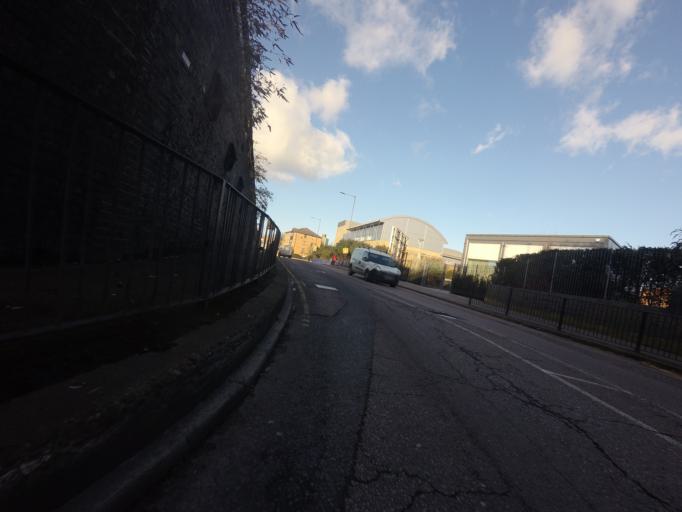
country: GB
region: England
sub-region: Greater London
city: Poplar
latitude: 51.5287
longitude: 0.0049
